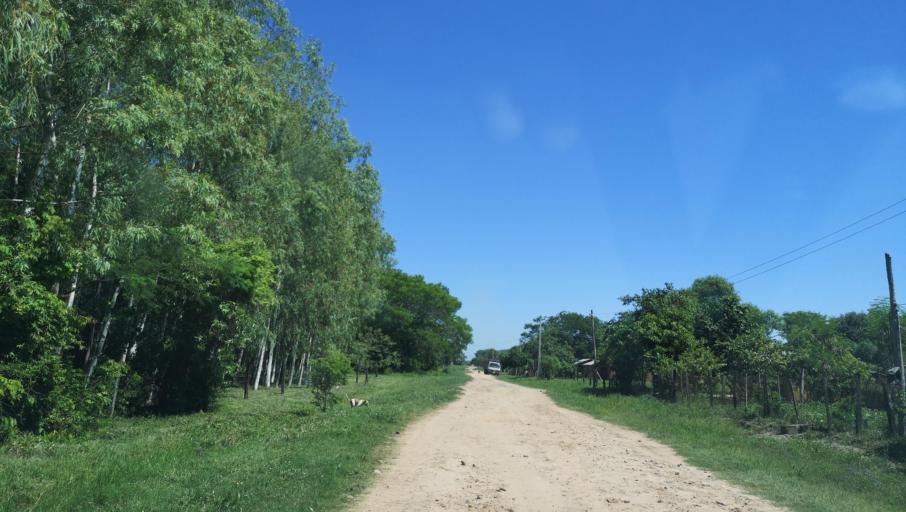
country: PY
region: Caaguazu
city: Carayao
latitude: -25.1939
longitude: -56.3948
